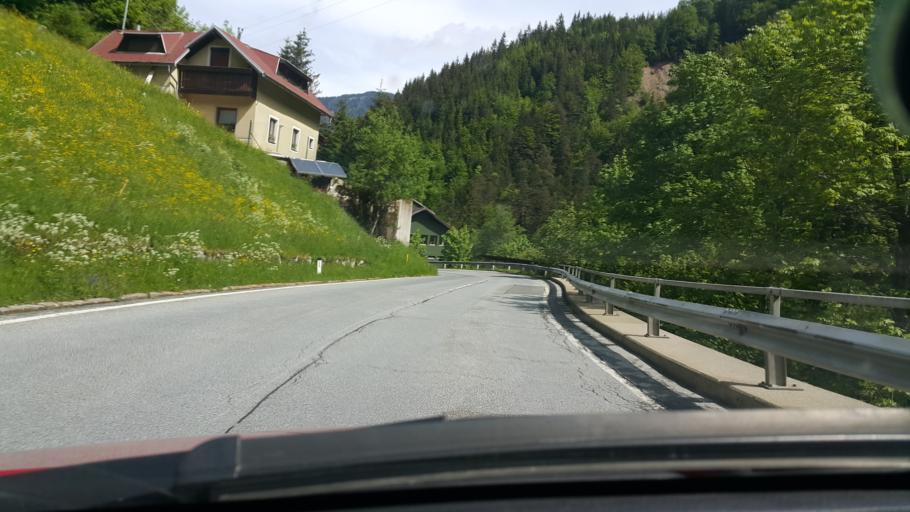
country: AT
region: Carinthia
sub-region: Politischer Bezirk Klagenfurt Land
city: Ferlach
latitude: 46.4597
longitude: 14.2589
